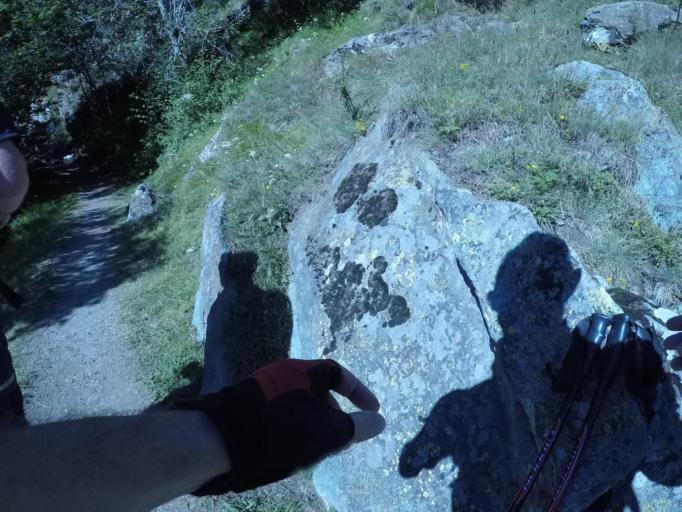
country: IT
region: Aosta Valley
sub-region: Valle d'Aosta
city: Valtournenche
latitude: 45.8744
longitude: 7.6118
